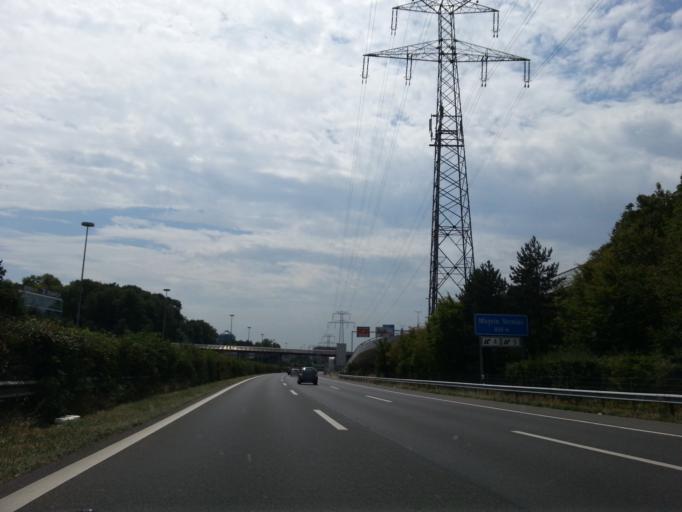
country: CH
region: Geneva
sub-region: Geneva
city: Les Avanchets
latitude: 46.2318
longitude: 6.1119
